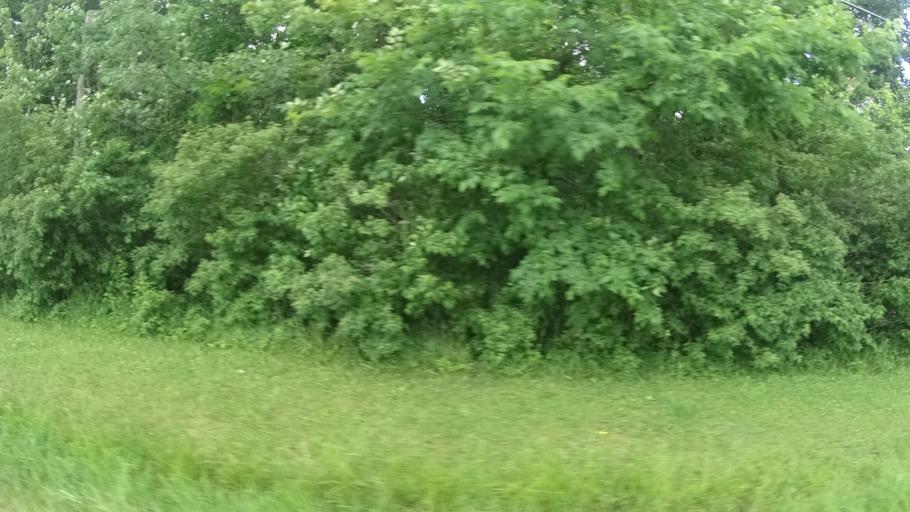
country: US
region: Ohio
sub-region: Huron County
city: Wakeman
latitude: 41.3084
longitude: -82.4325
